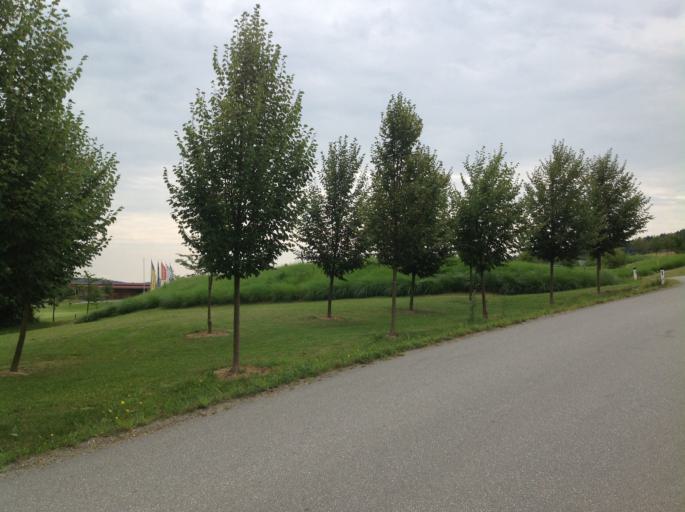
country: AT
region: Styria
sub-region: Politischer Bezirk Hartberg-Fuerstenfeld
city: Bad Waltersdorf
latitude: 47.1597
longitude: 16.0085
